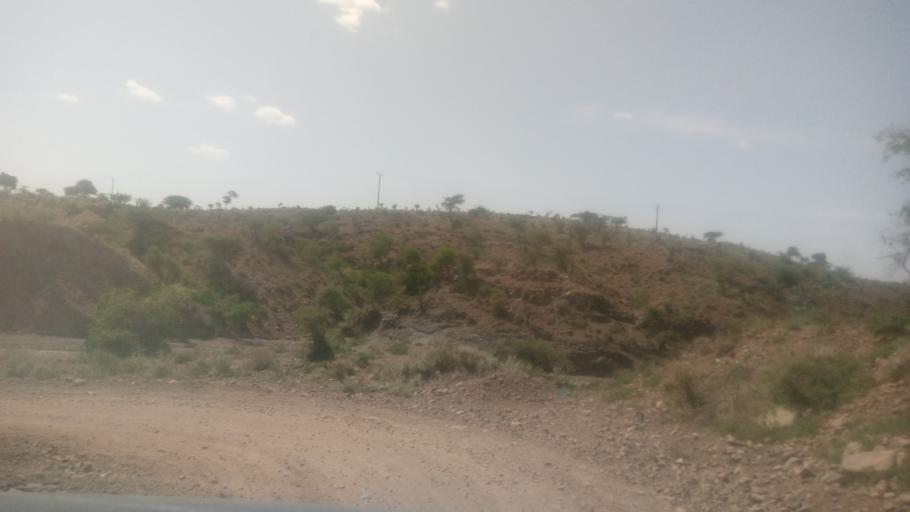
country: ET
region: Oromiya
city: Deder
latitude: 9.4901
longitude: 41.2696
